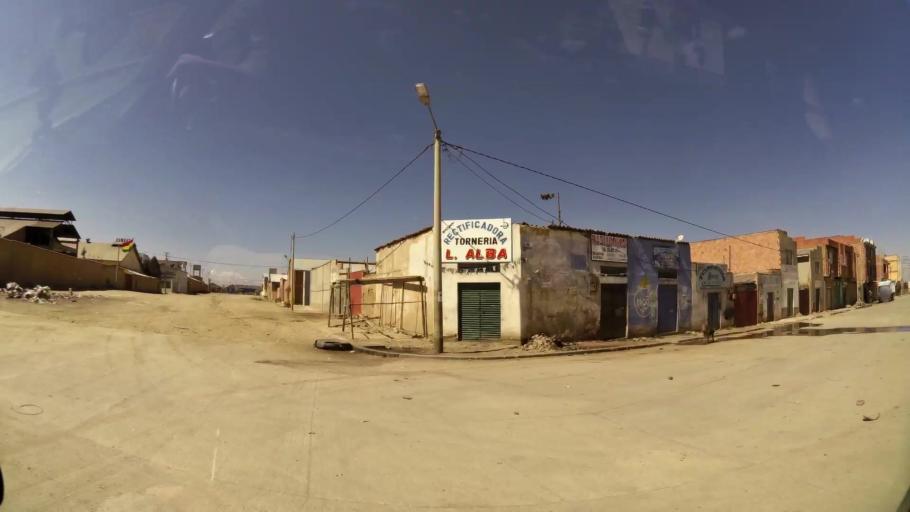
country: BO
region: La Paz
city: La Paz
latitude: -16.5483
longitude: -68.1815
